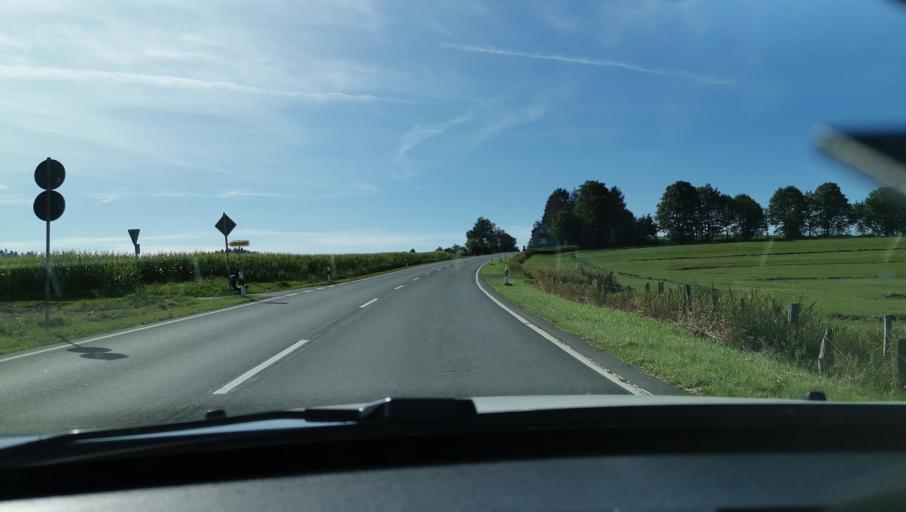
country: DE
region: North Rhine-Westphalia
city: Halver
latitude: 51.2140
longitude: 7.4873
